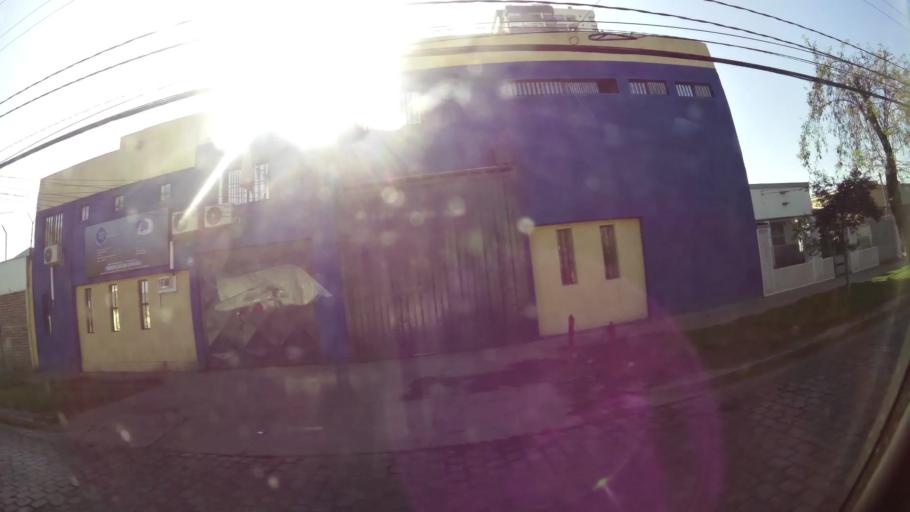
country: CL
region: Santiago Metropolitan
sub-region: Provincia de Santiago
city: Santiago
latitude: -33.4659
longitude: -70.6307
